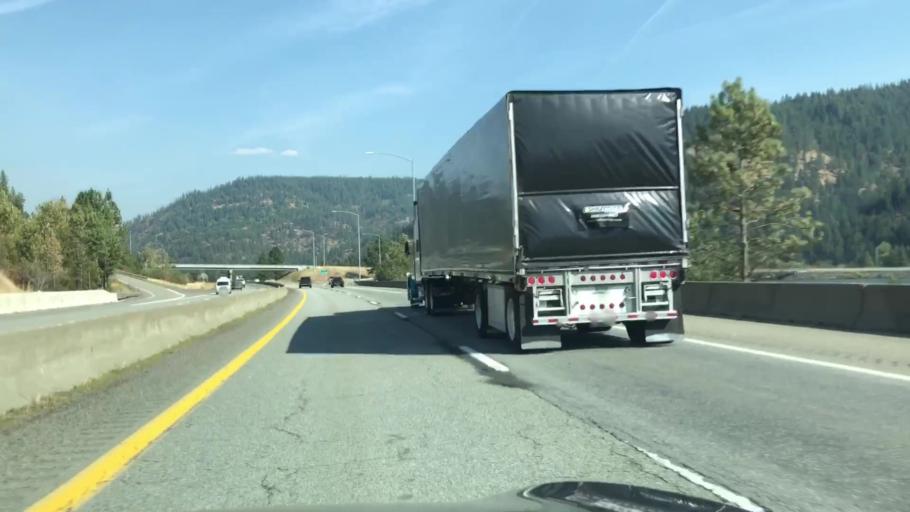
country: US
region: Idaho
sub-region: Kootenai County
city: Coeur d'Alene
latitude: 47.6235
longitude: -116.6541
